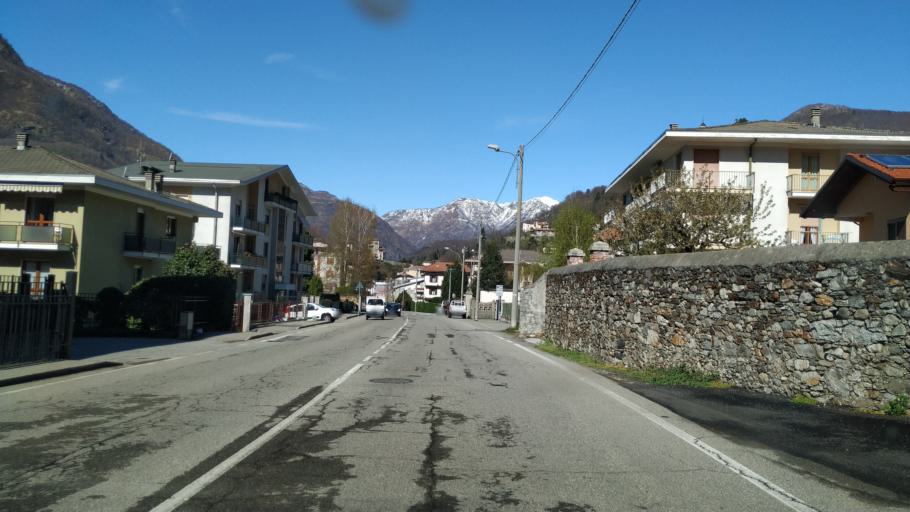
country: IT
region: Piedmont
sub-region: Provincia di Vercelli
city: Varallo
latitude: 45.8140
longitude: 8.2639
